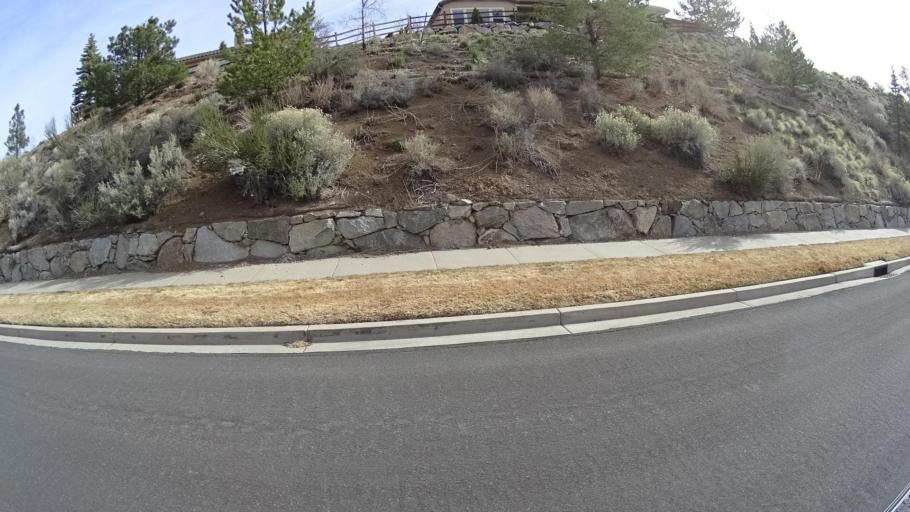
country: US
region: Nevada
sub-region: Washoe County
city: Mogul
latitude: 39.5334
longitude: -119.9166
